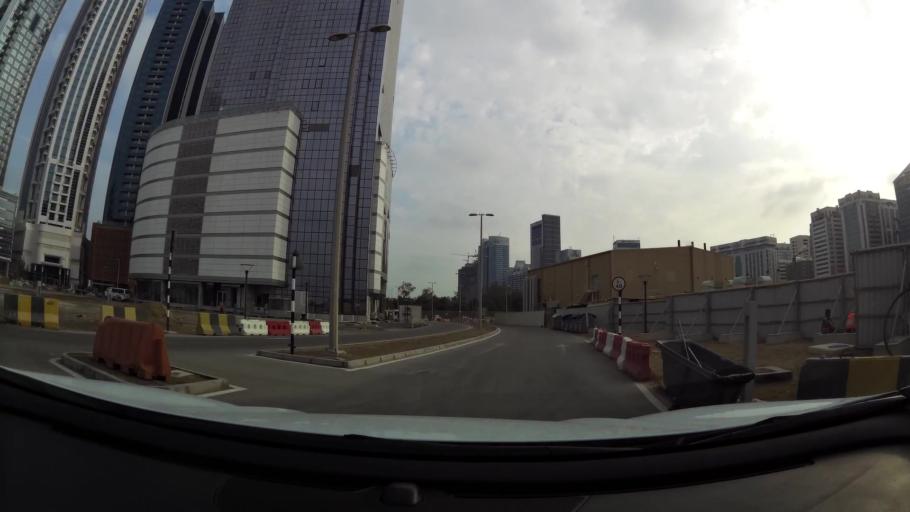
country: AE
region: Abu Dhabi
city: Abu Dhabi
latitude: 24.5025
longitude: 54.3702
